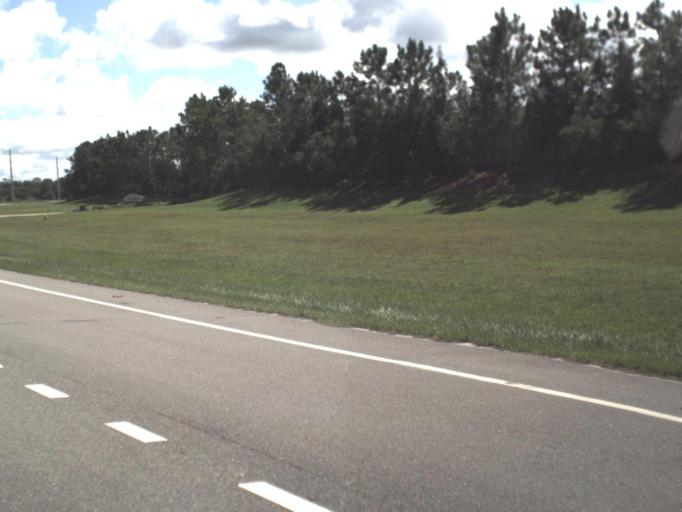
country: US
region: Florida
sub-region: Sarasota County
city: The Meadows
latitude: 27.4319
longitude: -82.3861
